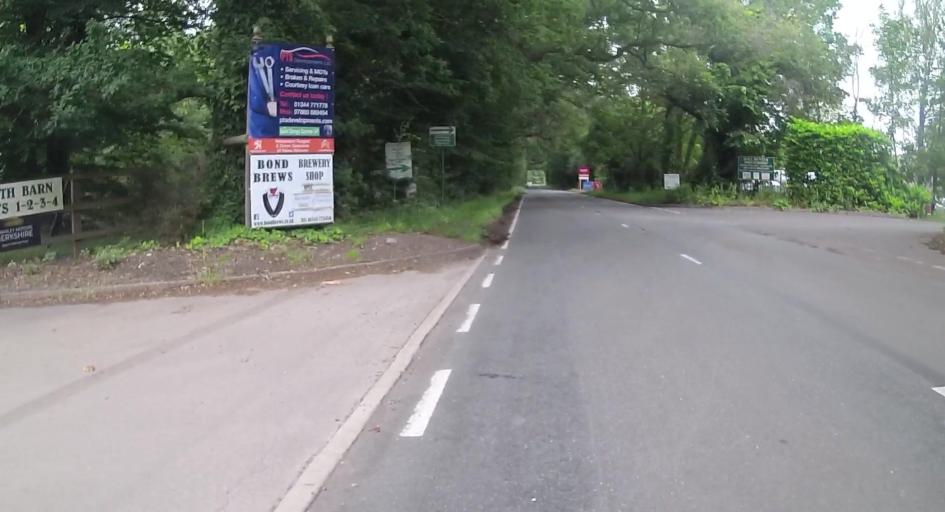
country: GB
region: England
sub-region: Wokingham
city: Wokingham
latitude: 51.3896
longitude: -0.8169
